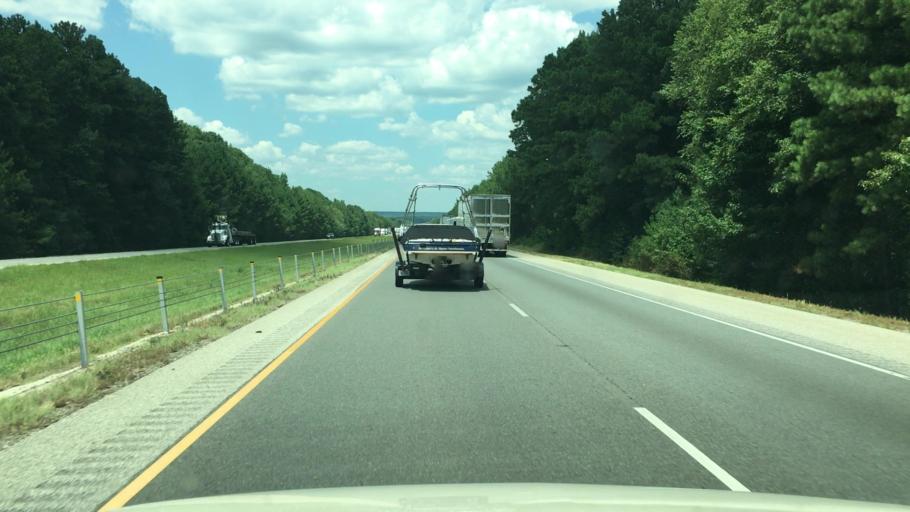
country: US
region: Arkansas
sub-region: Clark County
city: Arkadelphia
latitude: 34.1489
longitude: -93.0788
